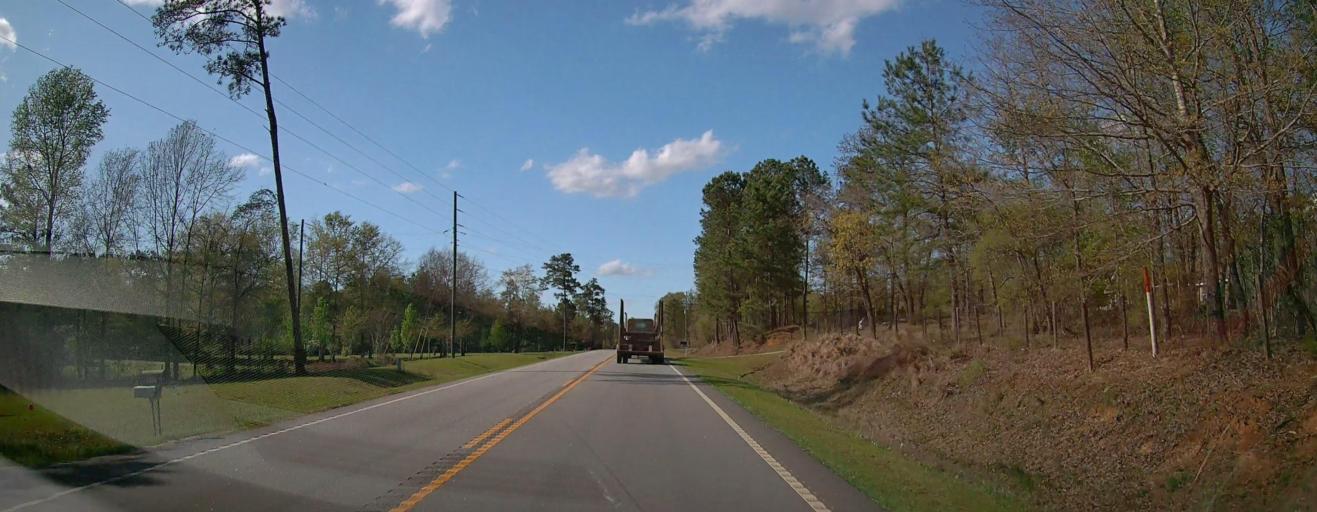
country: US
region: Georgia
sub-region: Baldwin County
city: Hardwick
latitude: 33.0635
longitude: -83.1322
